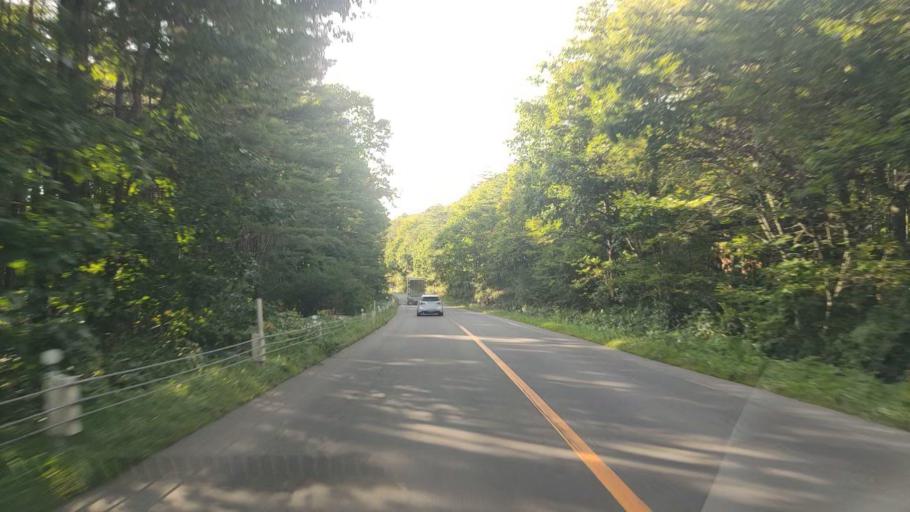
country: JP
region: Nagano
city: Ueda
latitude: 36.4879
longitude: 138.4202
